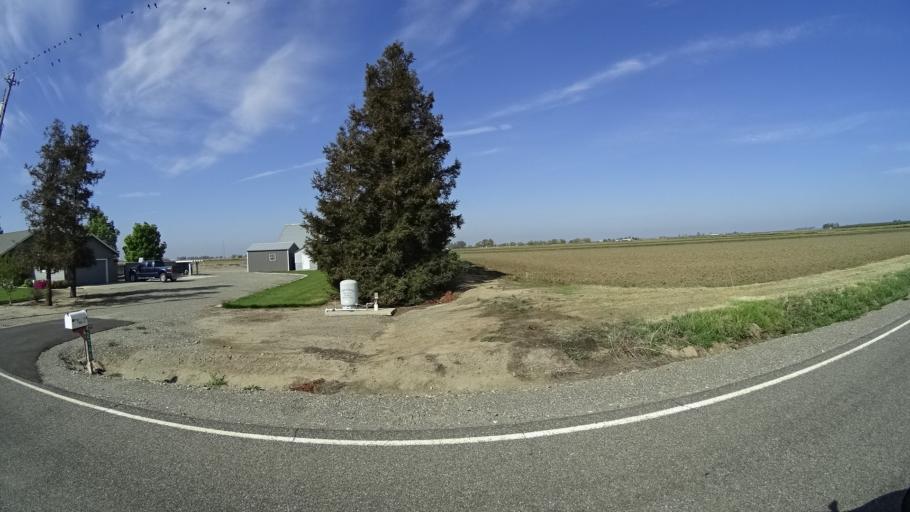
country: US
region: California
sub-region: Glenn County
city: Hamilton City
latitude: 39.5998
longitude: -122.0368
